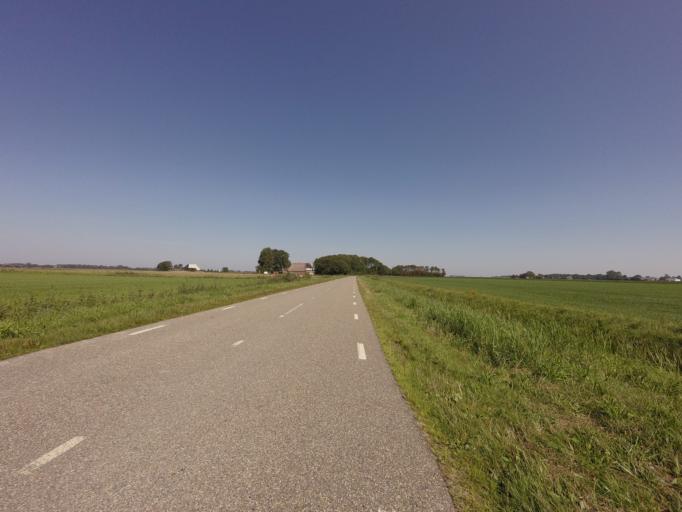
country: NL
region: Friesland
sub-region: Gemeente Dongeradeel
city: Ternaard
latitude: 53.3646
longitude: 5.9811
